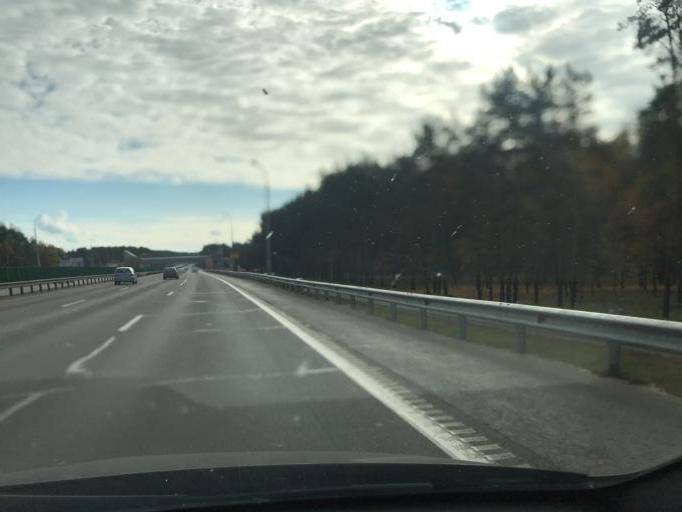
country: BY
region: Minsk
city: Vyaliki Trastsyanets
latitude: 53.8940
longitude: 27.6921
